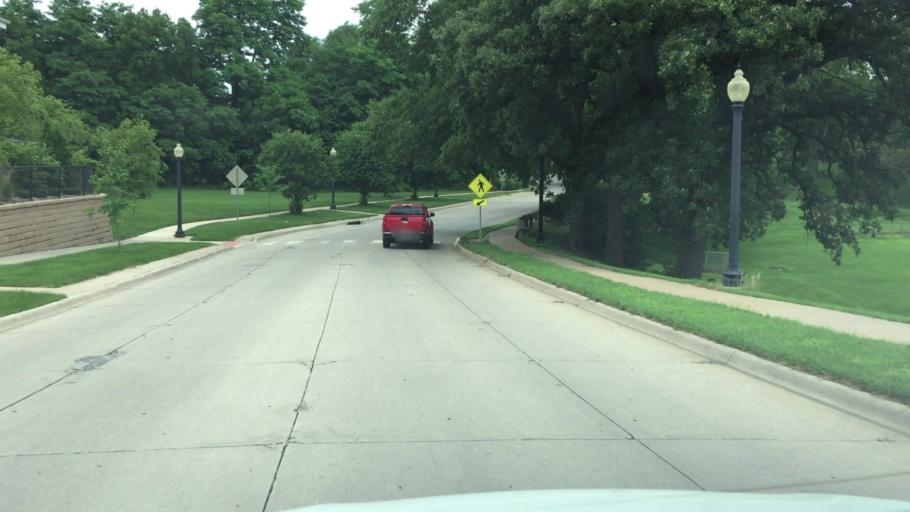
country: US
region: Iowa
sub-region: Jasper County
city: Newton
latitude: 41.7046
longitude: -93.0537
